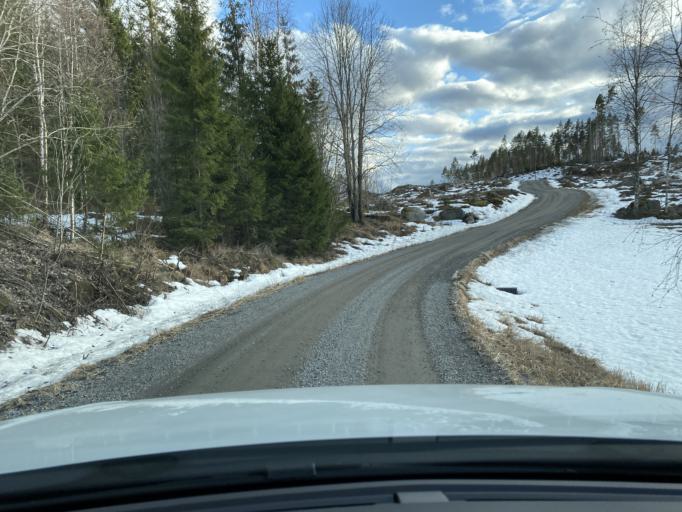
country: FI
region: Pirkanmaa
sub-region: Lounais-Pirkanmaa
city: Mouhijaervi
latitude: 61.4375
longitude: 22.9664
